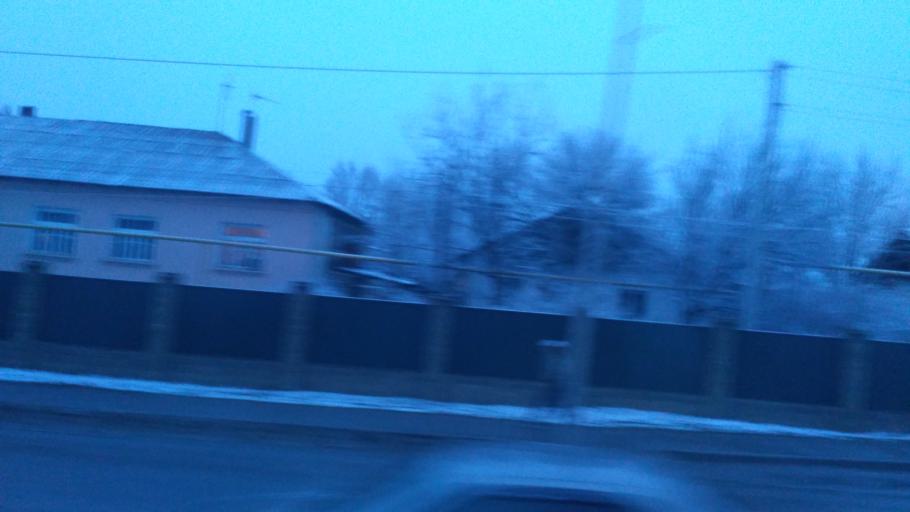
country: KZ
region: Ongtustik Qazaqstan
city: Shymkent
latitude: 42.3717
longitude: 69.5052
